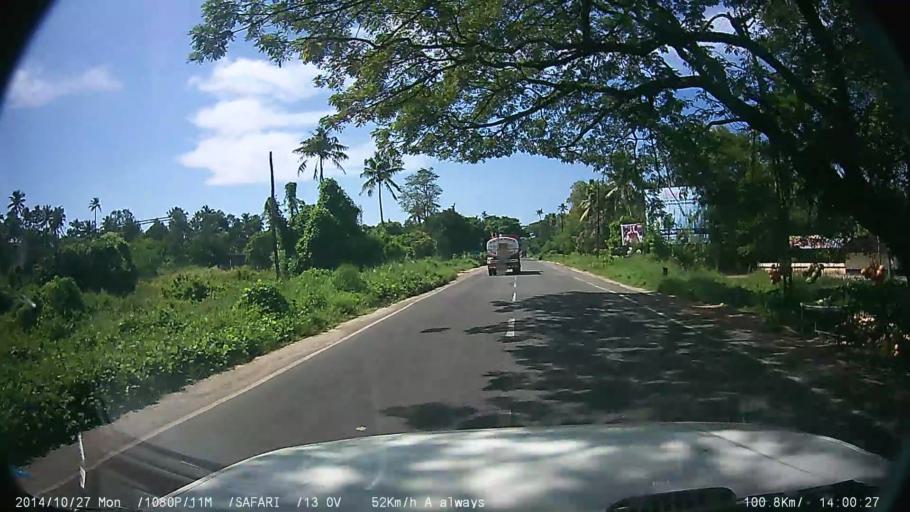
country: IN
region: Kerala
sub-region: Alappuzha
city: Vayalar
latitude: 9.6929
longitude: 76.3237
